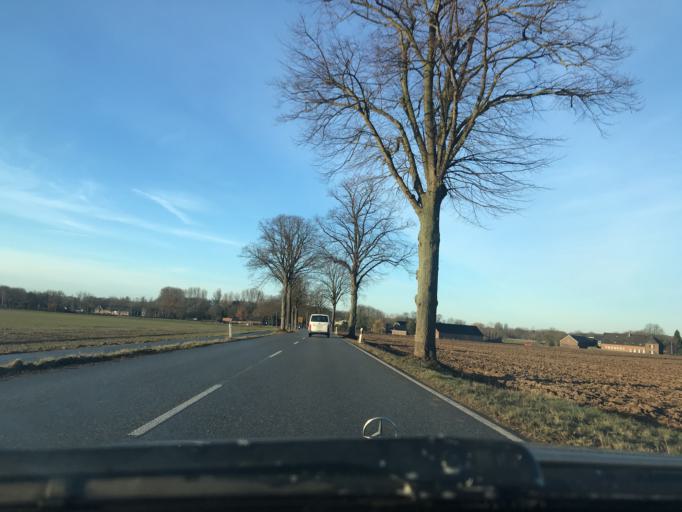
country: DE
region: North Rhine-Westphalia
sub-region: Regierungsbezirk Dusseldorf
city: Krefeld
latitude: 51.4135
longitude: 6.5656
